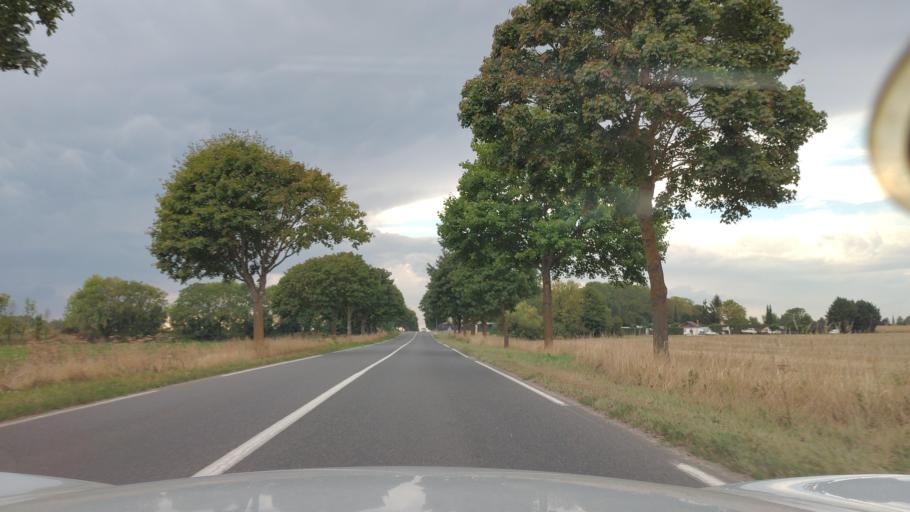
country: FR
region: Ile-de-France
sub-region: Departement de Seine-et-Marne
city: Grisy-Suisnes
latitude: 48.6739
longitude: 2.6794
